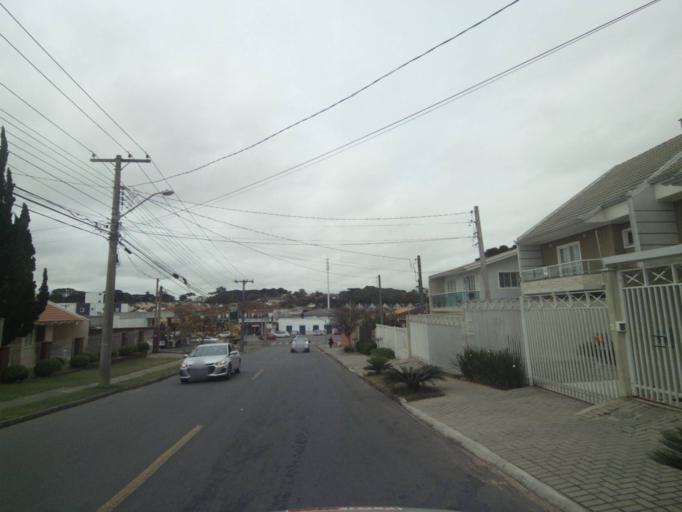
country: BR
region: Parana
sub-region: Pinhais
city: Pinhais
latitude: -25.4795
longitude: -49.2263
